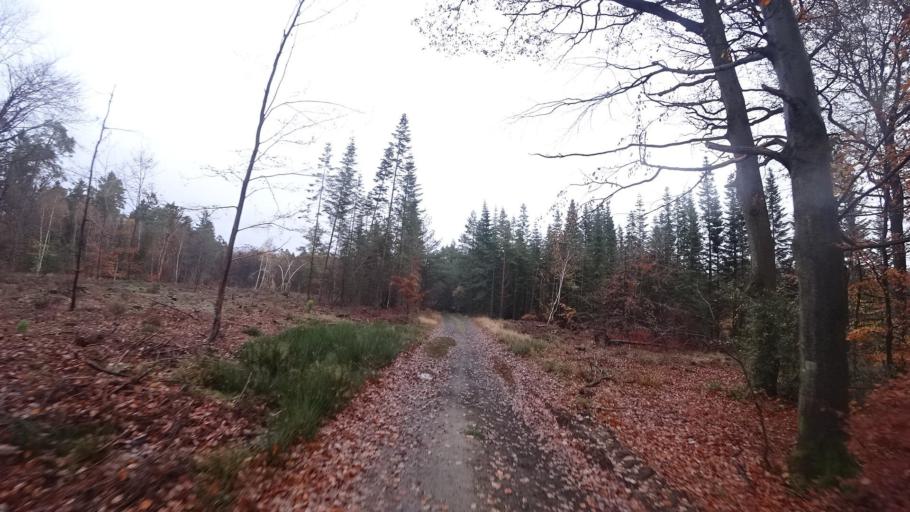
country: DE
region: Rheinland-Pfalz
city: Schalkenbach
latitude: 50.4979
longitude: 7.1213
